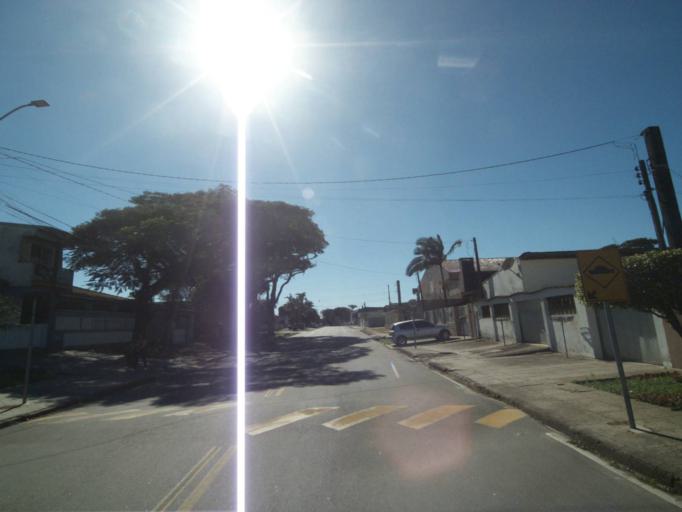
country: BR
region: Parana
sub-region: Paranagua
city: Paranagua
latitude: -25.5321
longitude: -48.5281
